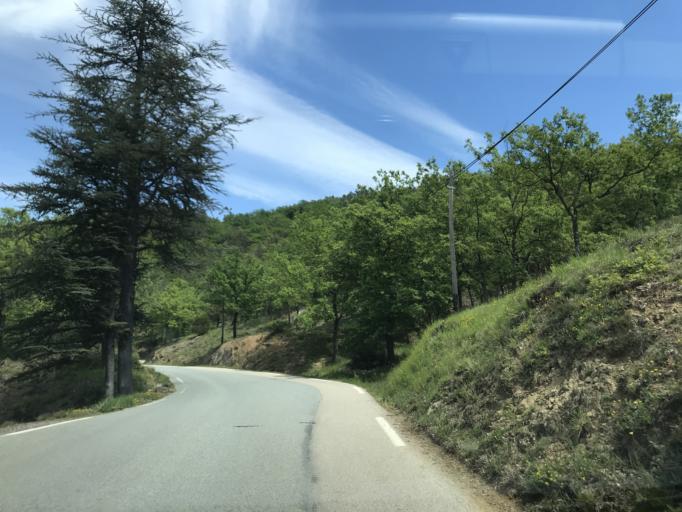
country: FR
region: Provence-Alpes-Cote d'Azur
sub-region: Departement du Var
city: Montauroux
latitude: 43.5832
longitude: 6.8144
